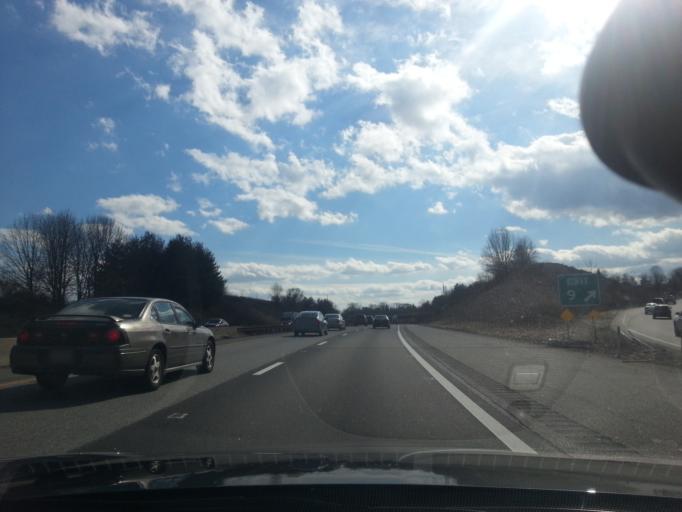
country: US
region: Pennsylvania
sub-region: Delaware County
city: Broomall
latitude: 39.9814
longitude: -75.3387
